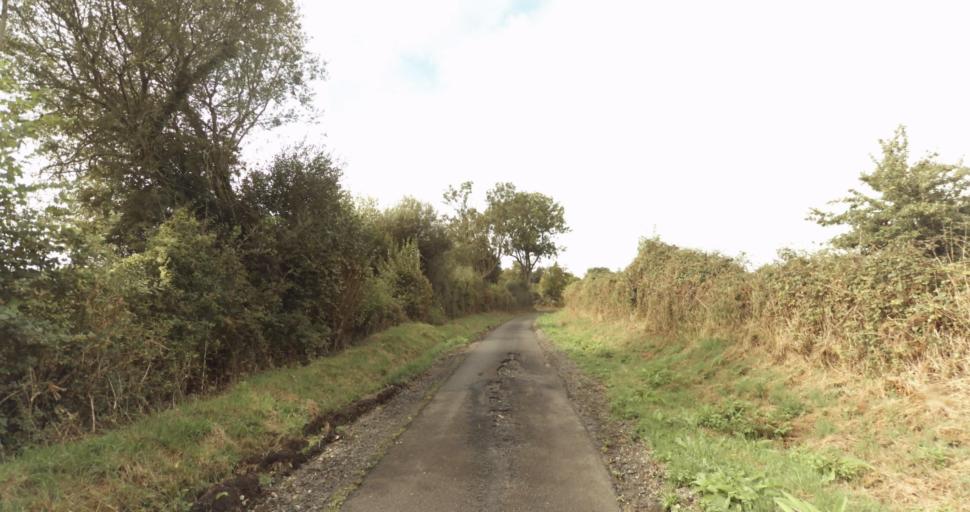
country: FR
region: Lower Normandy
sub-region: Departement de l'Orne
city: Vimoutiers
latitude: 48.8513
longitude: 0.2073
